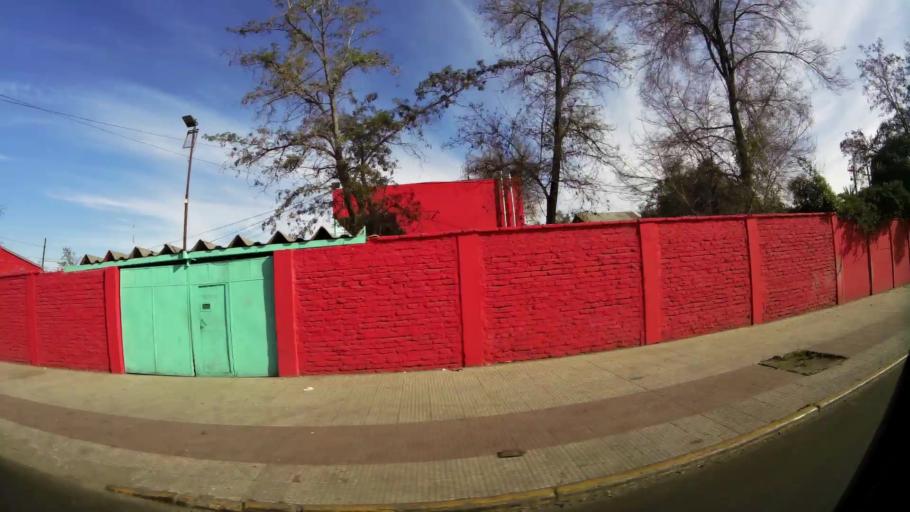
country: CL
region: Santiago Metropolitan
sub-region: Provincia de Santiago
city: Santiago
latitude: -33.4616
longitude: -70.6851
